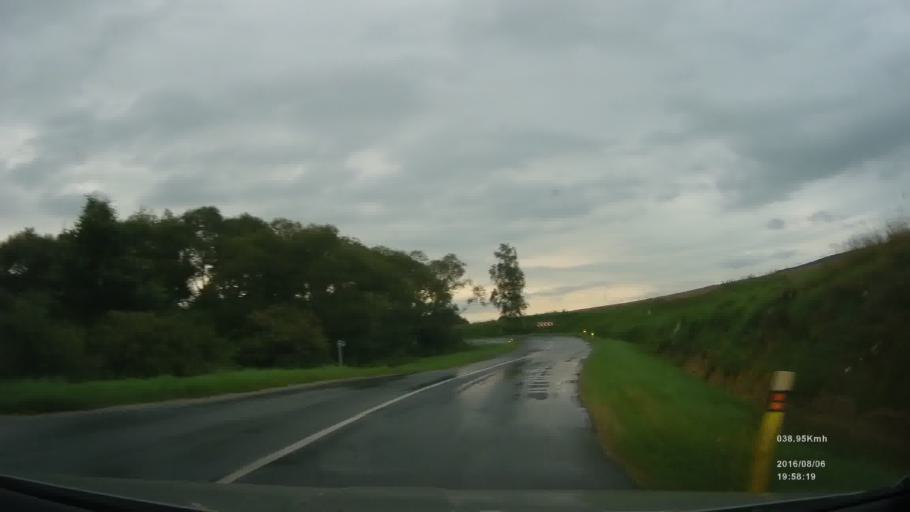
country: SK
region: Presovsky
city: Svidnik
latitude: 49.2700
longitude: 21.5803
